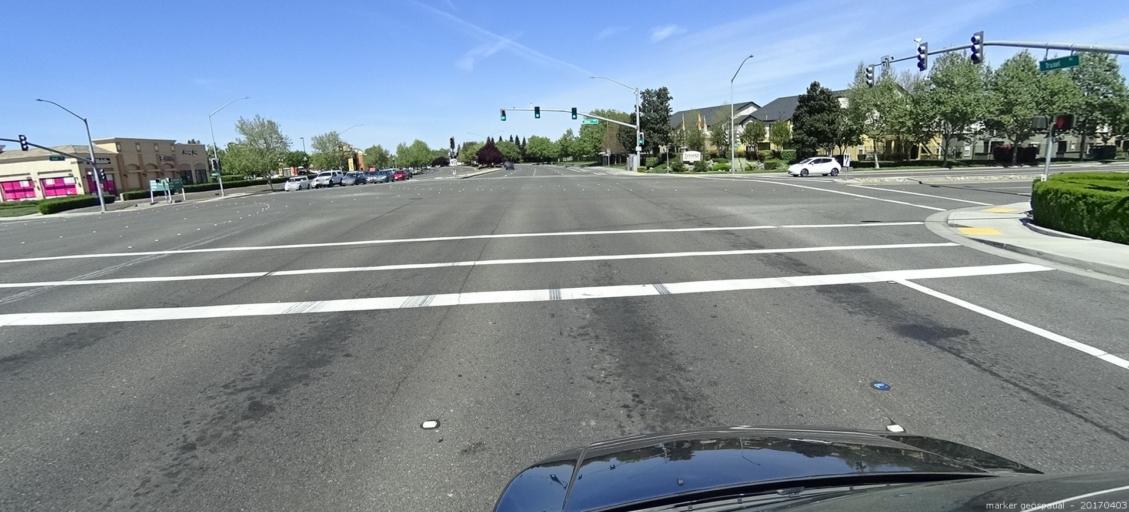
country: US
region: California
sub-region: Sacramento County
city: Sacramento
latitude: 38.6465
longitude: -121.5089
